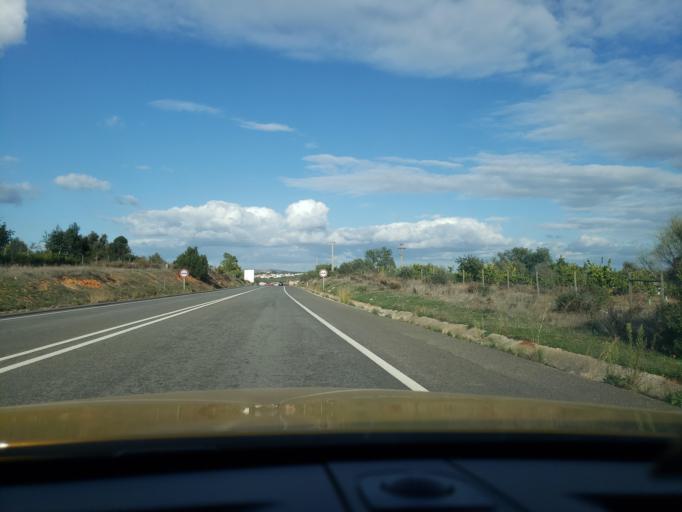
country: PT
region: Faro
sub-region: Silves
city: Silves
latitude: 37.1642
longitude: -8.4442
